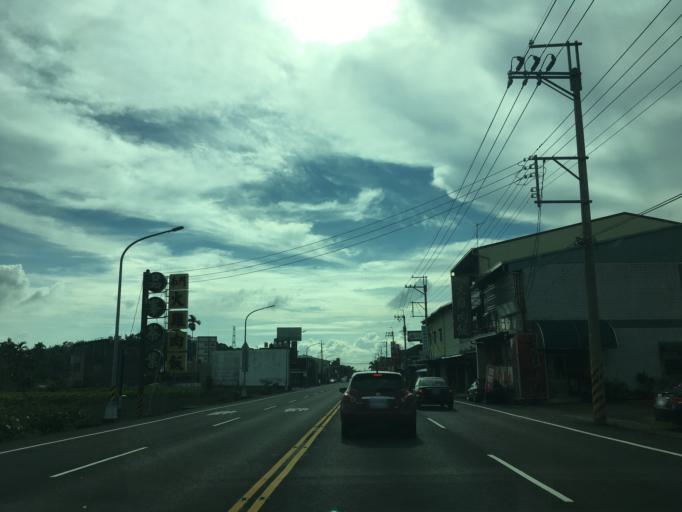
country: TW
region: Taiwan
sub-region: Chiayi
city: Jiayi Shi
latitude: 23.4435
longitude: 120.5091
